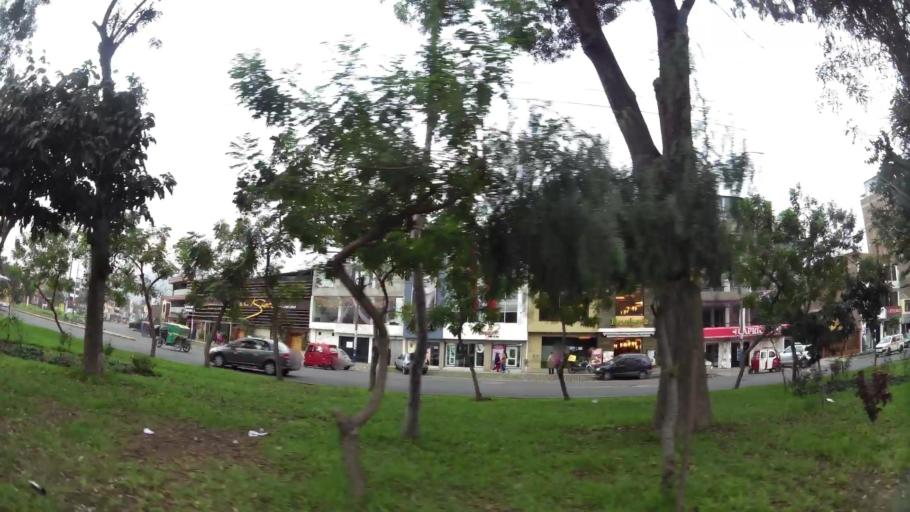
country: PE
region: Lima
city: Lima
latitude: -12.0088
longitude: -77.0111
